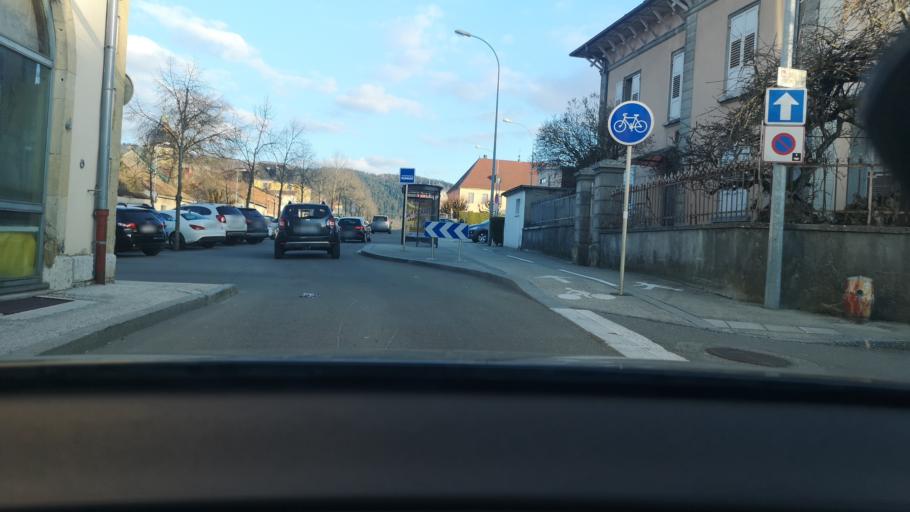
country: FR
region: Franche-Comte
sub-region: Departement du Doubs
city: Pontarlier
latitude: 46.9034
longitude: 6.3527
